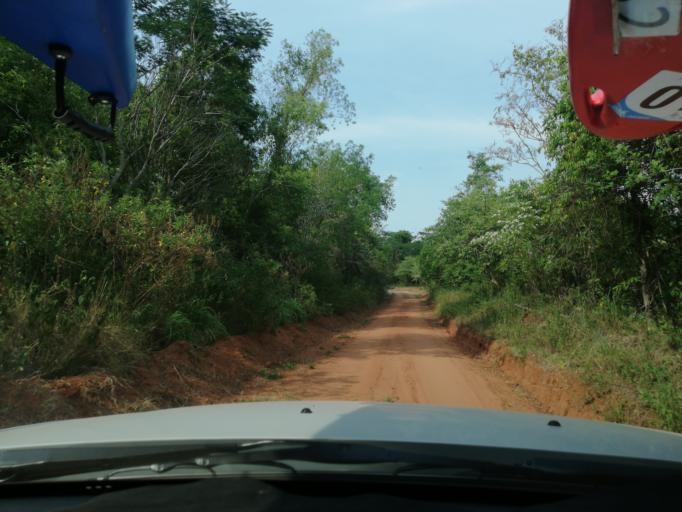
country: AR
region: Misiones
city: Santa Ana
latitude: -27.3064
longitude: -55.5850
